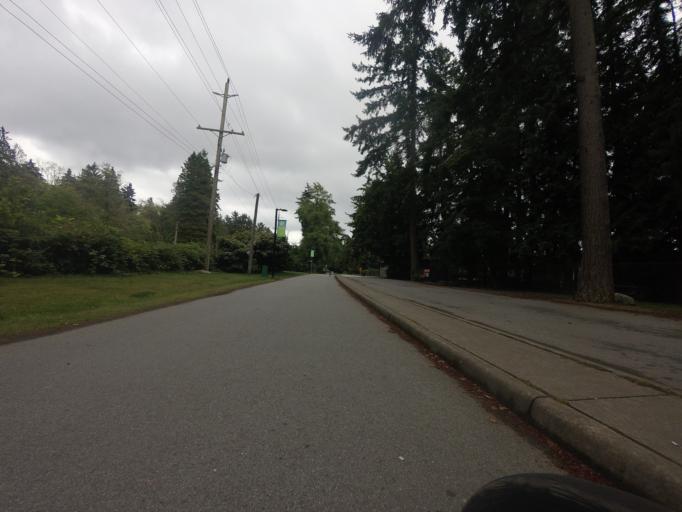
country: CA
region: British Columbia
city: West End
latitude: 49.3248
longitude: -123.1473
